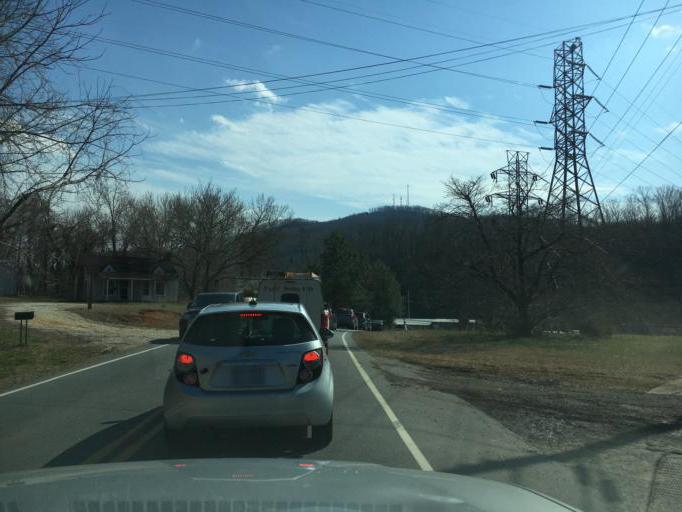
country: US
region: North Carolina
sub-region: McDowell County
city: Marion
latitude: 35.6763
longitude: -81.9934
